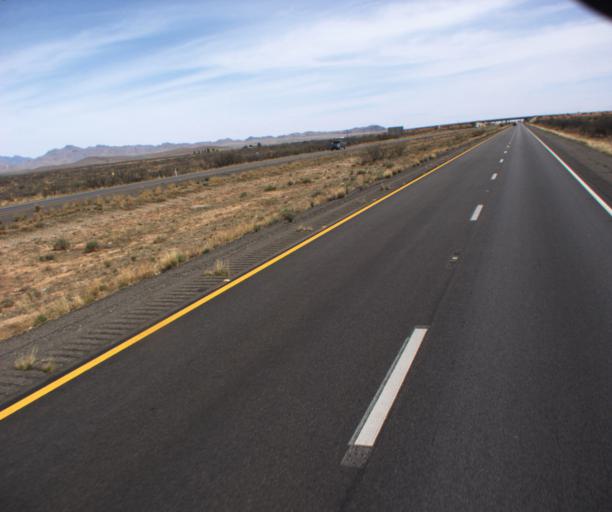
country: US
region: Arizona
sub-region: Cochise County
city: Willcox
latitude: 32.3000
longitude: -109.8059
